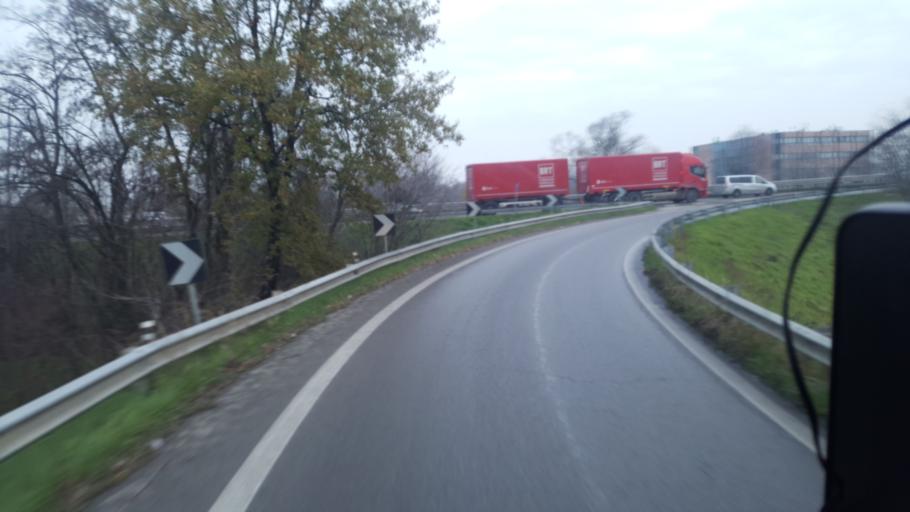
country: IT
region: Emilia-Romagna
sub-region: Provincia di Parma
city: Parma
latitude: 44.8212
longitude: 10.3116
